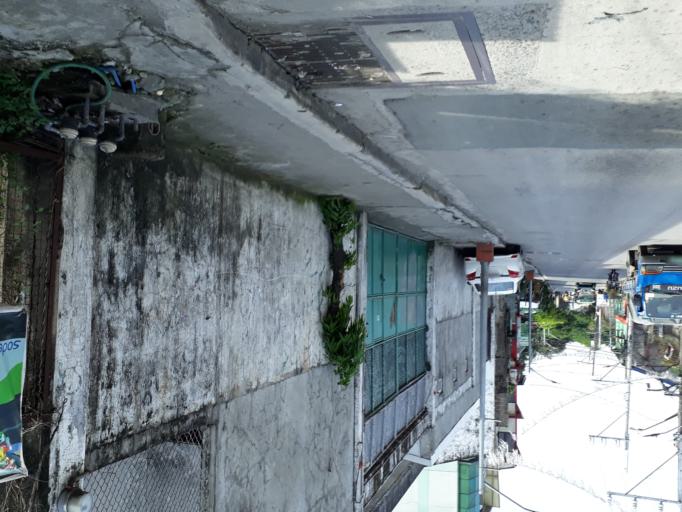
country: PH
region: Calabarzon
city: Bagong Pagasa
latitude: 14.6728
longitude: 121.0053
